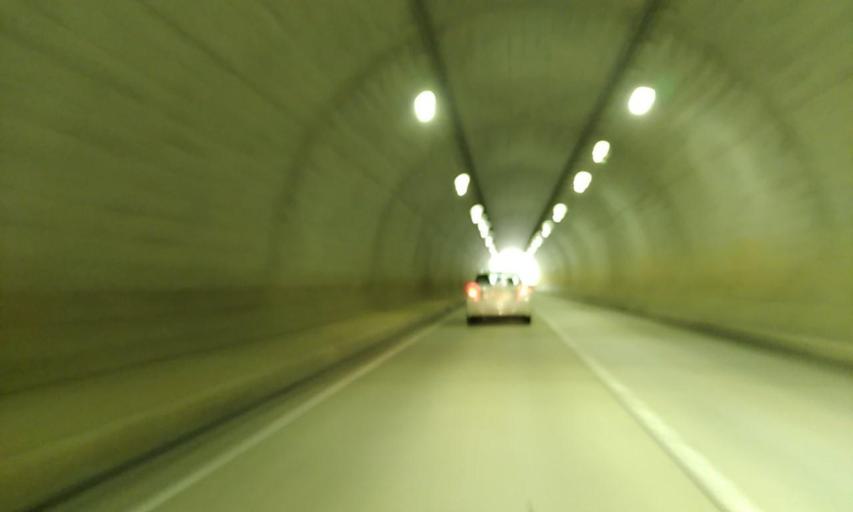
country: JP
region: Fukui
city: Obama
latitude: 35.5259
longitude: 135.8032
